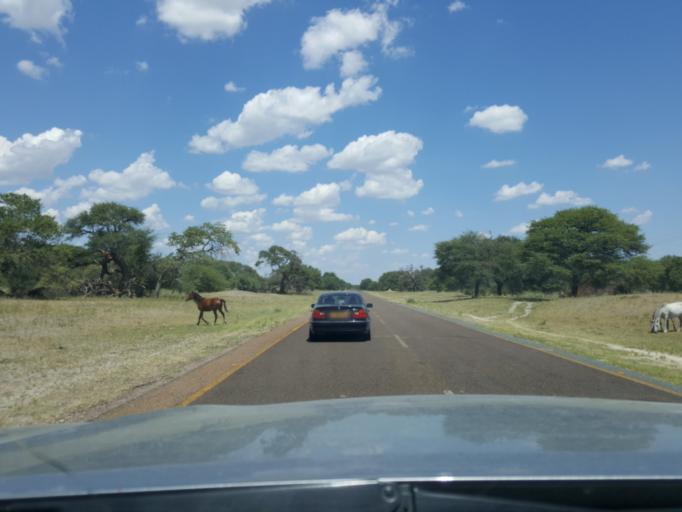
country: BW
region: North West
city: Maun
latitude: -20.1785
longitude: 23.2504
